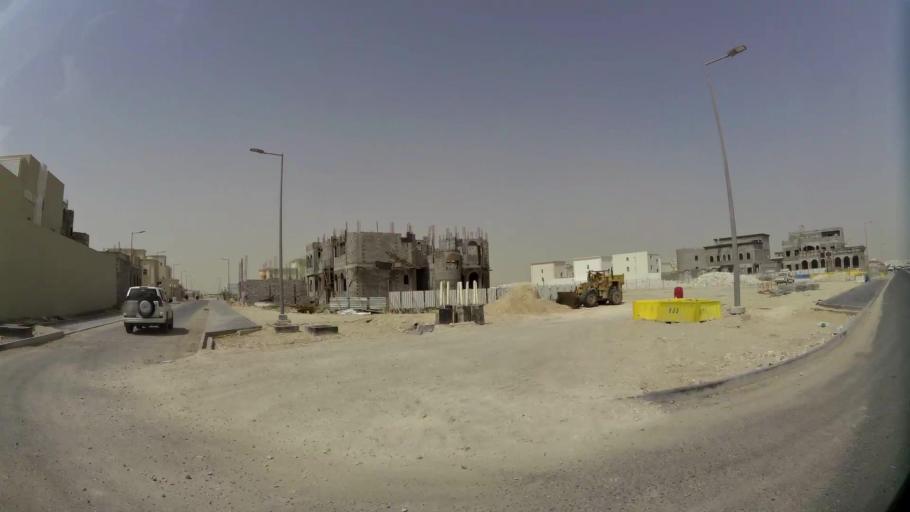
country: QA
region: Baladiyat ar Rayyan
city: Ar Rayyan
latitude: 25.2594
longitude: 51.3694
